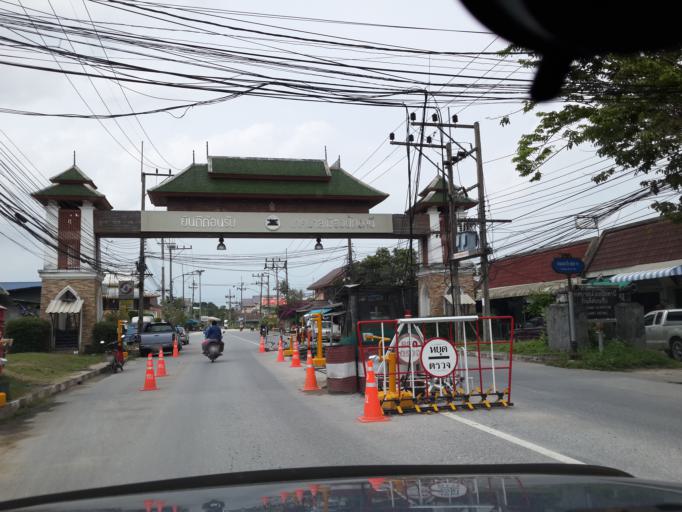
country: TH
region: Pattani
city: Pattani
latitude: 6.8520
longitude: 101.2531
